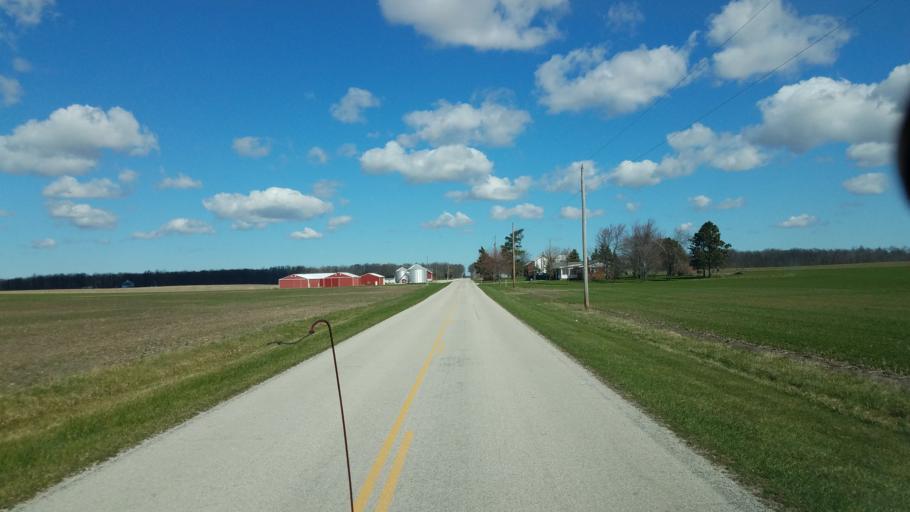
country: US
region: Ohio
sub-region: Sandusky County
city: Mount Carmel
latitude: 41.1740
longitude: -82.9381
